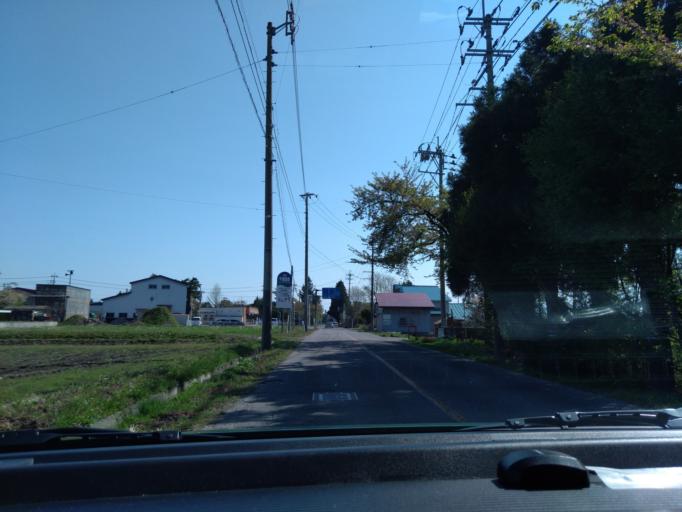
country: JP
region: Akita
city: Omagari
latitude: 39.4682
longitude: 140.5832
